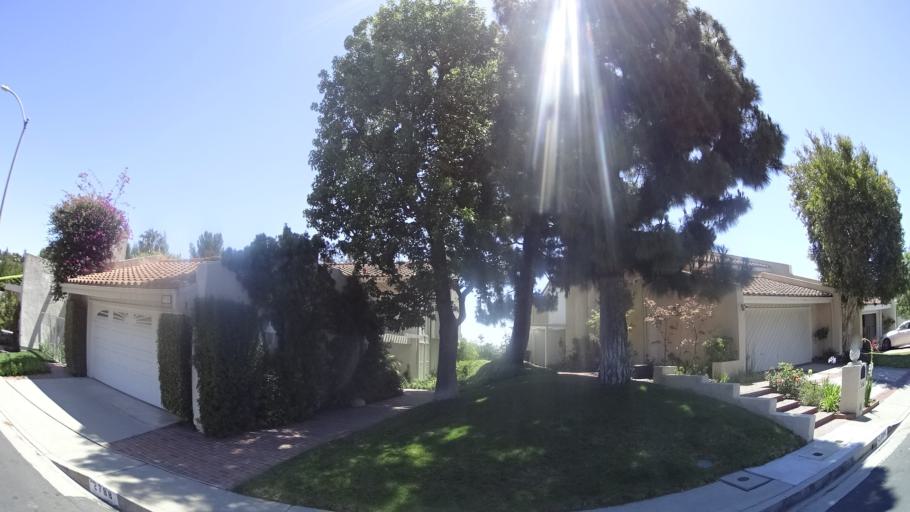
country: US
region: California
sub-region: Los Angeles County
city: Sherman Oaks
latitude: 34.1241
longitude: -118.4497
